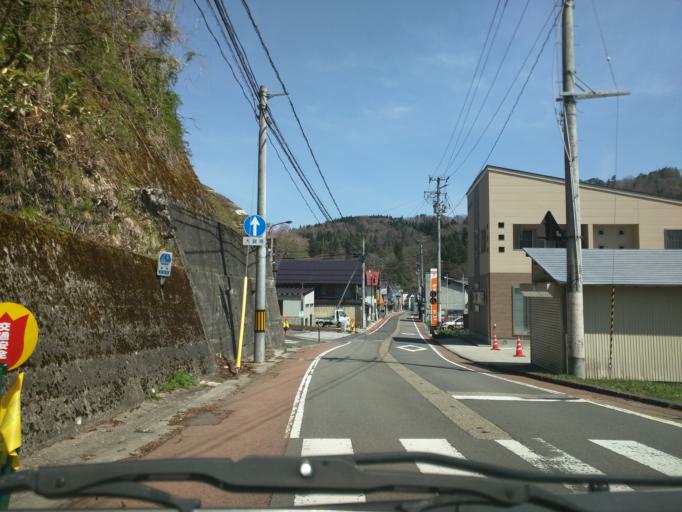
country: JP
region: Fukushima
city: Kitakata
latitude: 37.5283
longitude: 139.7250
